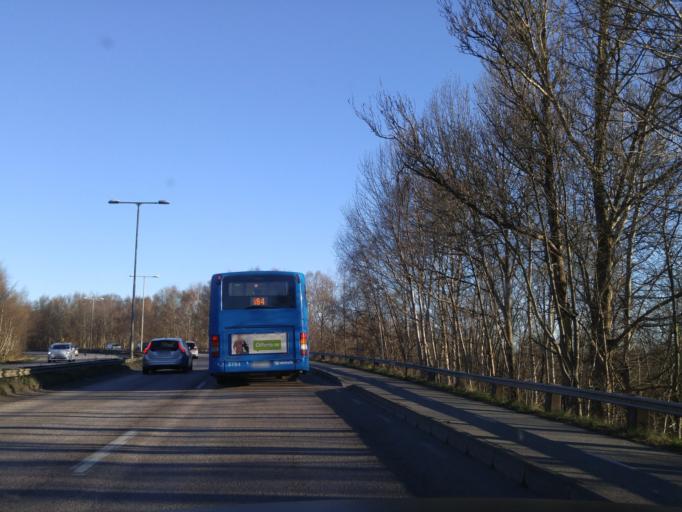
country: SE
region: Vaestra Goetaland
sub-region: Goteborg
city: Majorna
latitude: 57.6786
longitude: 11.9127
